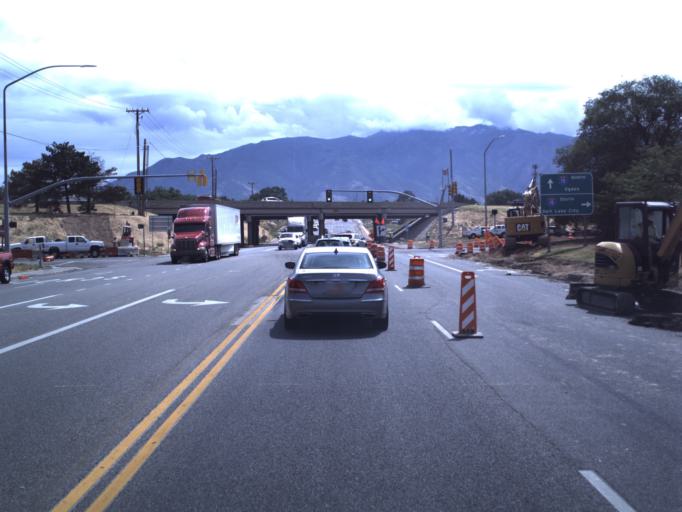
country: US
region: Utah
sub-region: Davis County
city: Clearfield
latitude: 41.1035
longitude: -112.0062
